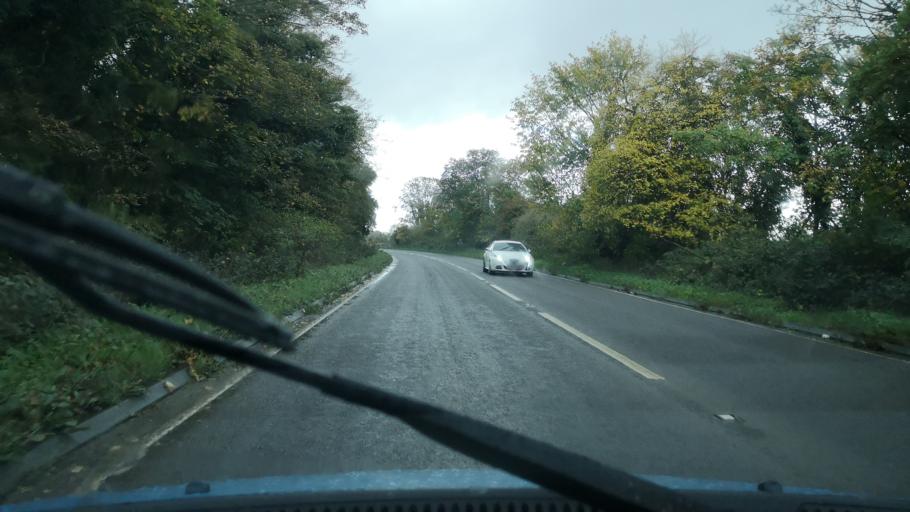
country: GB
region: England
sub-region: North Lincolnshire
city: Crowle
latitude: 53.5871
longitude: -0.8244
